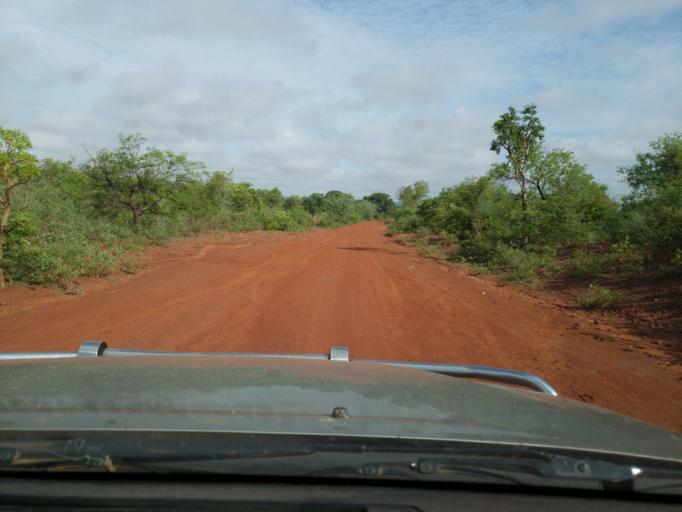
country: ML
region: Sikasso
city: Koutiala
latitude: 12.3895
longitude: -5.9739
